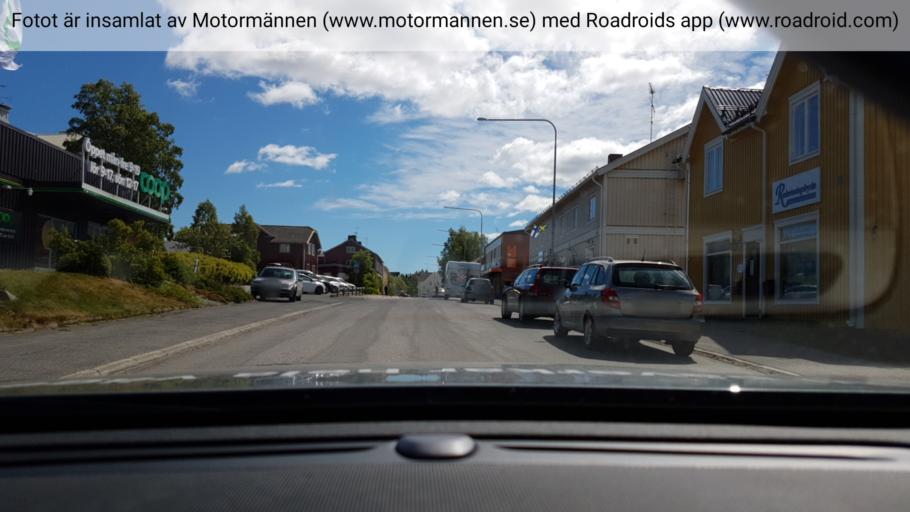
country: SE
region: Vaesterbotten
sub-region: Skelleftea Kommun
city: Burea
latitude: 64.3705
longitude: 21.3112
